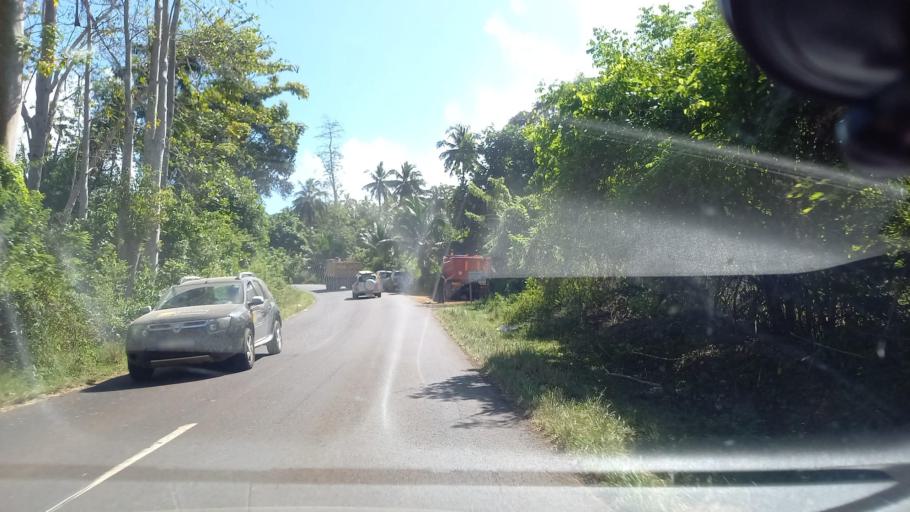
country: YT
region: M'Tsangamouji
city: M'Tsangamouji
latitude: -12.7555
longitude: 45.0952
